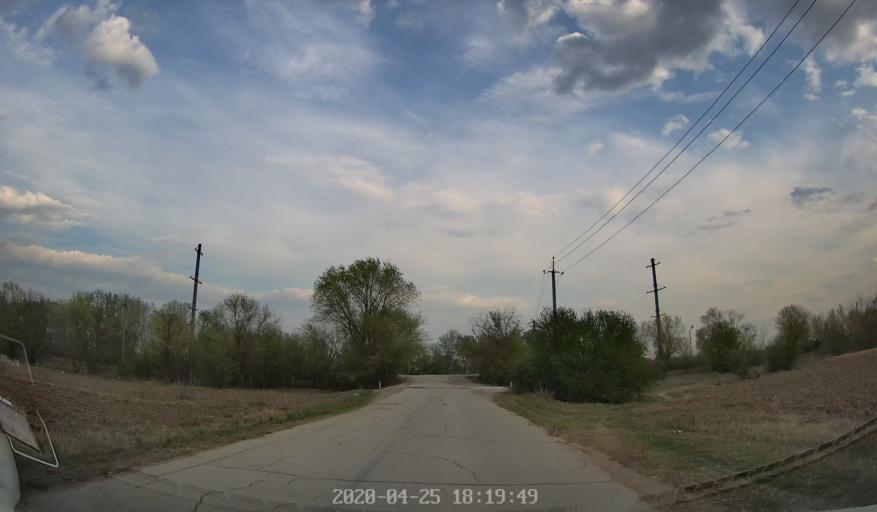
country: MD
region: Criuleni
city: Criuleni
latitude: 47.1579
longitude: 29.1324
